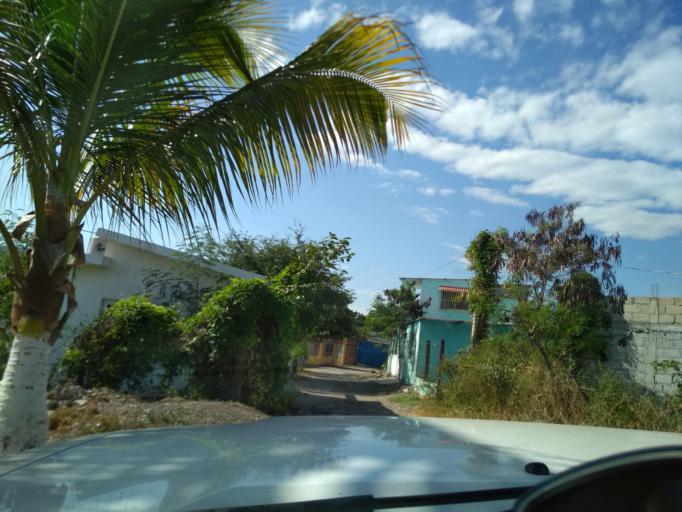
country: MX
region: Veracruz
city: Rinconada
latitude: 19.3570
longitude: -96.5630
